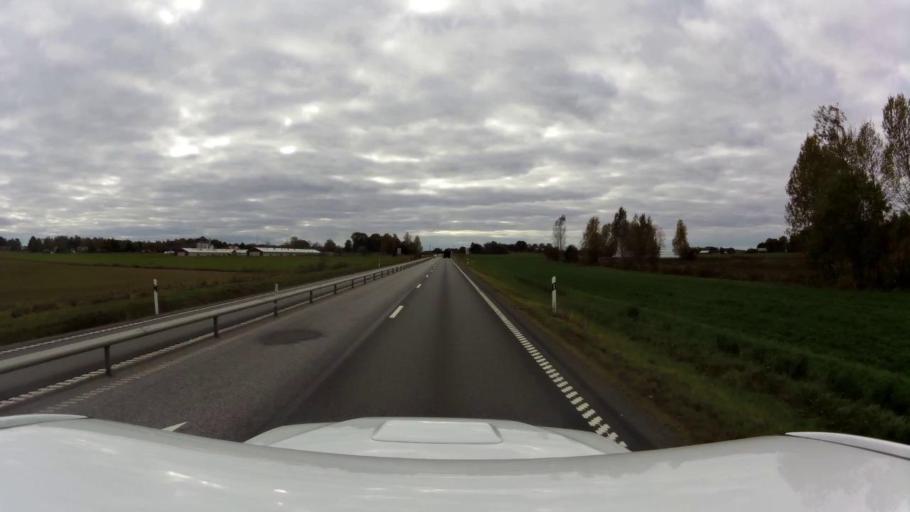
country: SE
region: OEstergoetland
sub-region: Linkopings Kommun
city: Malmslatt
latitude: 58.3468
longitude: 15.5511
